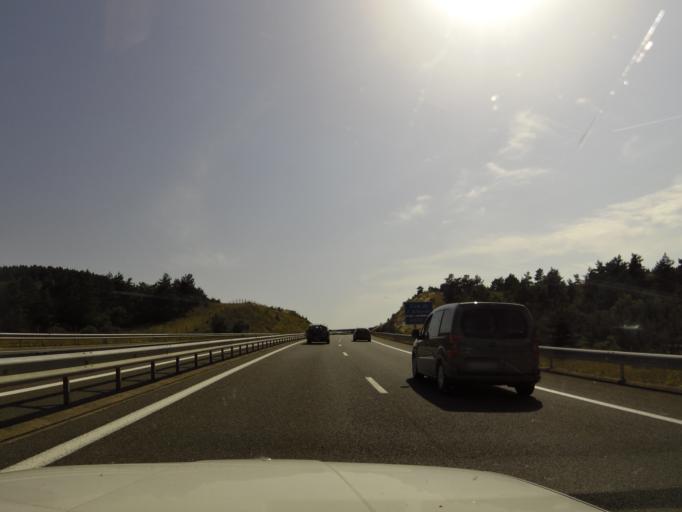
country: FR
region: Midi-Pyrenees
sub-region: Departement de l'Aveyron
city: Severac-le-Chateau
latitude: 44.3578
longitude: 3.1145
